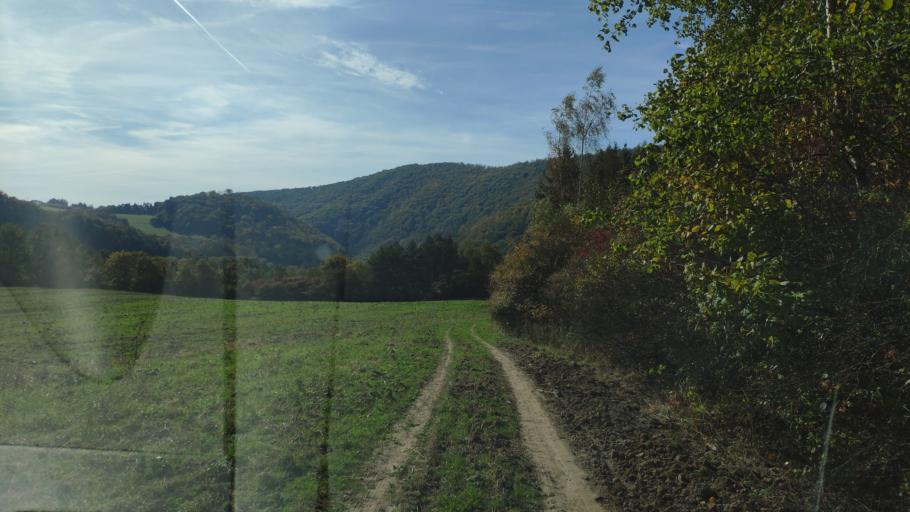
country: SK
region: Presovsky
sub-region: Okres Presov
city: Presov
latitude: 48.8821
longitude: 21.2286
